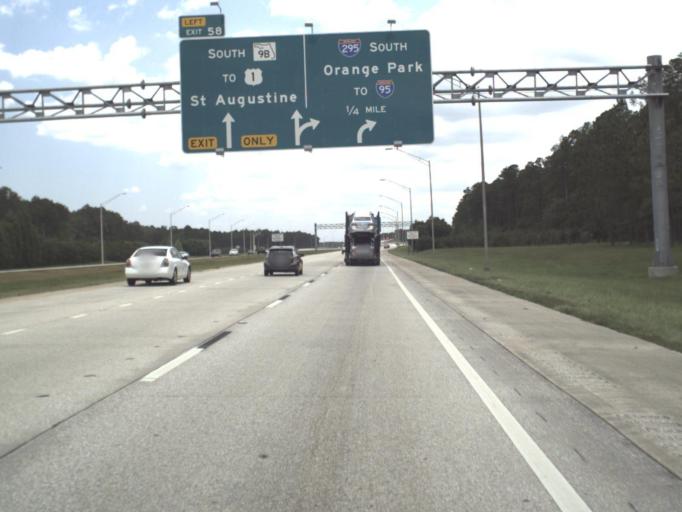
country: US
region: Florida
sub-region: Saint Johns County
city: Palm Valley
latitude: 30.1893
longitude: -81.5139
